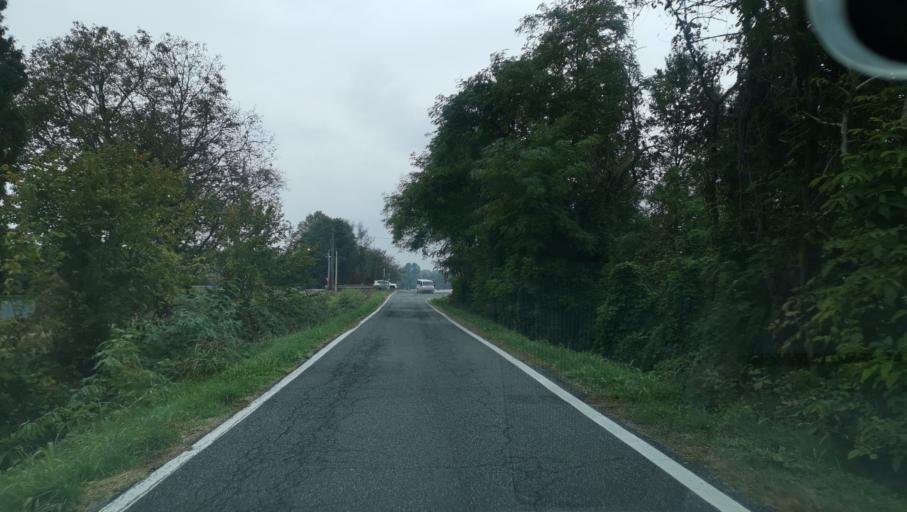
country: IT
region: Piedmont
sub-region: Provincia di Torino
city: San Raffaele Cimena
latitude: 45.1394
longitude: 7.8380
